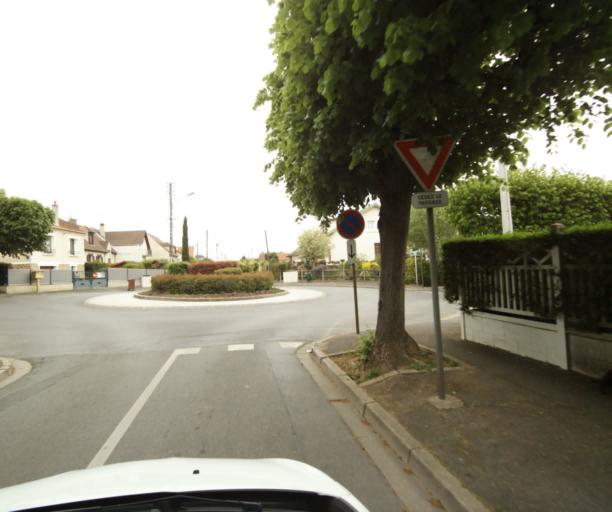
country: FR
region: Ile-de-France
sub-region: Departement de Seine-et-Marne
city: Torcy
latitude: 48.8539
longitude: 2.6457
